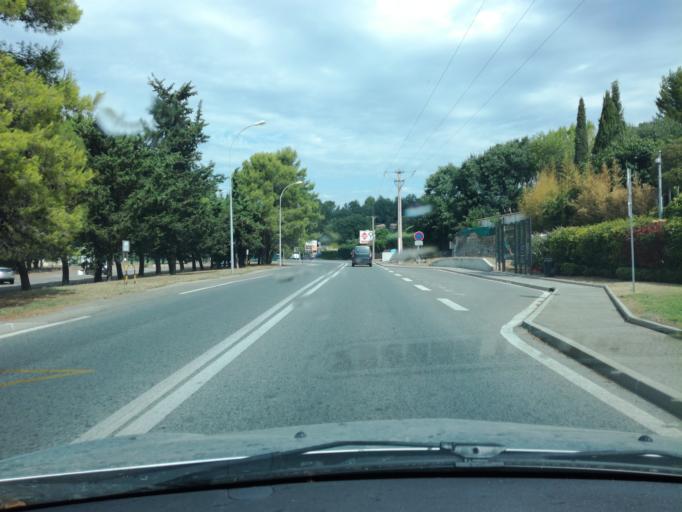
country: FR
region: Provence-Alpes-Cote d'Azur
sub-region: Departement du Var
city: Draguignan
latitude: 43.5254
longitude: 6.4602
